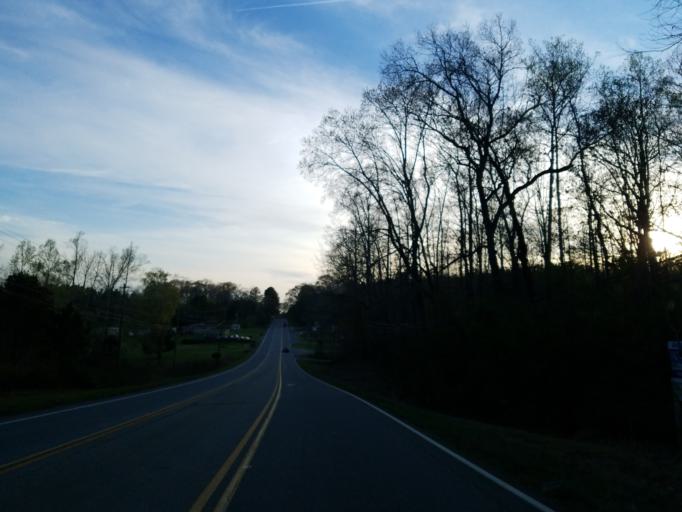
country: US
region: Georgia
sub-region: Cherokee County
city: Canton
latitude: 34.2862
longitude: -84.4341
